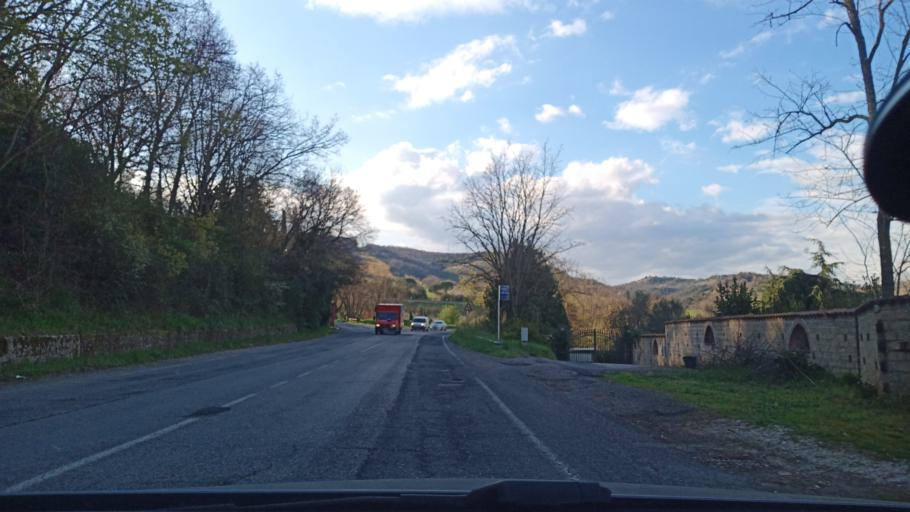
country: IT
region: Latium
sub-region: Citta metropolitana di Roma Capitale
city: Fiano Romano
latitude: 42.1798
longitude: 12.6063
